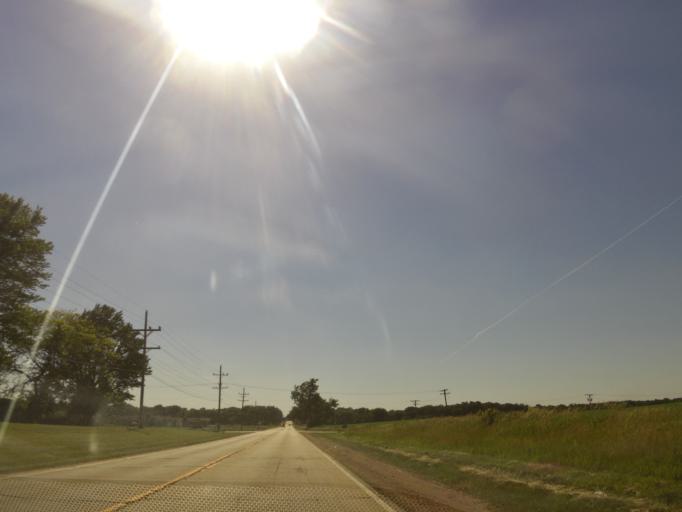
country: US
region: Illinois
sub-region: Ogle County
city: Davis Junction
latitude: 42.1005
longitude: -89.0314
